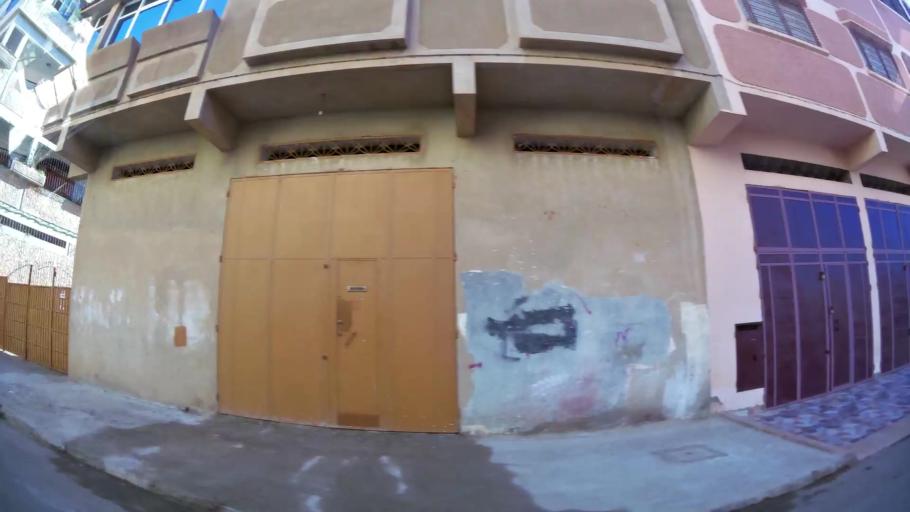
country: MA
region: Oriental
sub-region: Berkane-Taourirt
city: Berkane
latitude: 34.9327
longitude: -2.3356
